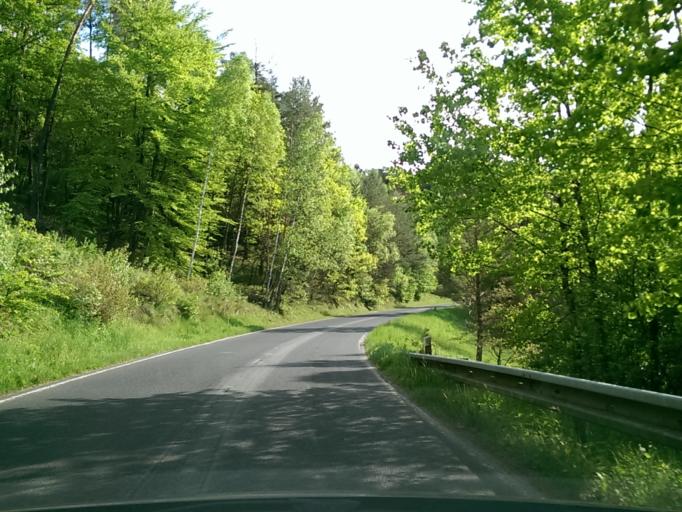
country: CZ
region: Central Bohemia
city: Bakov nad Jizerou
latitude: 50.4948
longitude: 14.8915
